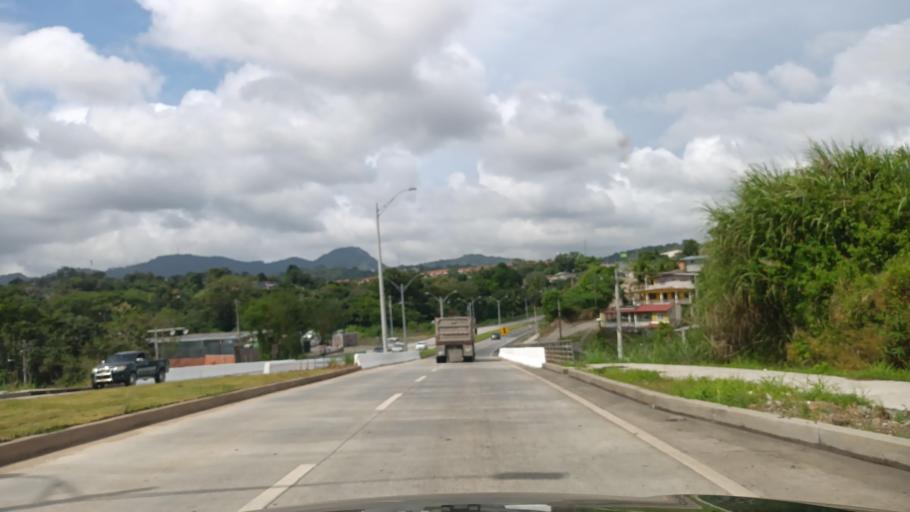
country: PA
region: Panama
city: Las Cumbres
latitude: 9.0990
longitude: -79.5121
